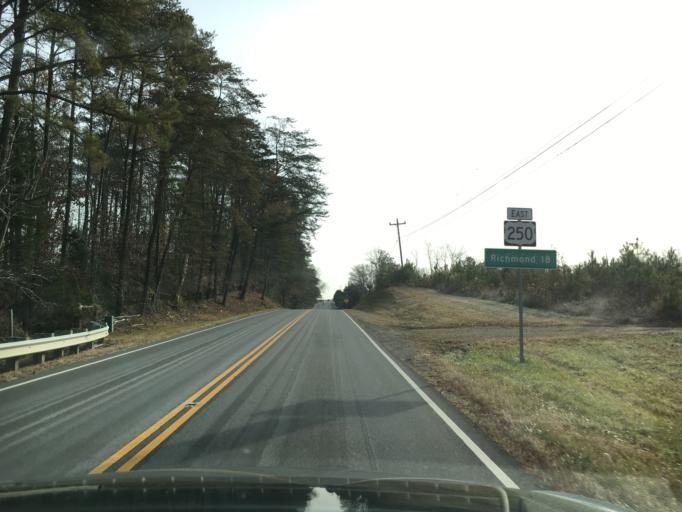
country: US
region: Virginia
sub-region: Henrico County
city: Short Pump
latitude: 37.6731
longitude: -77.6971
